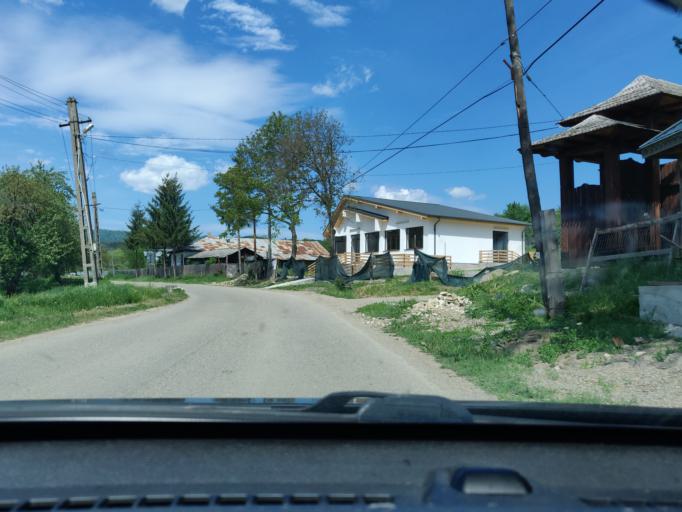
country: RO
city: Vizantea-Manastireasca
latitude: 45.9821
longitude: 26.7942
